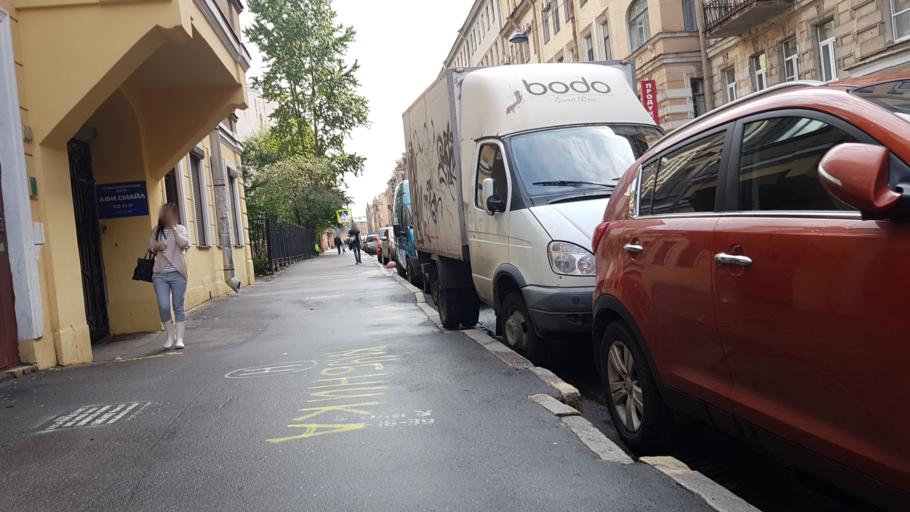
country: RU
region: St.-Petersburg
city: Centralniy
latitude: 59.9262
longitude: 30.3550
